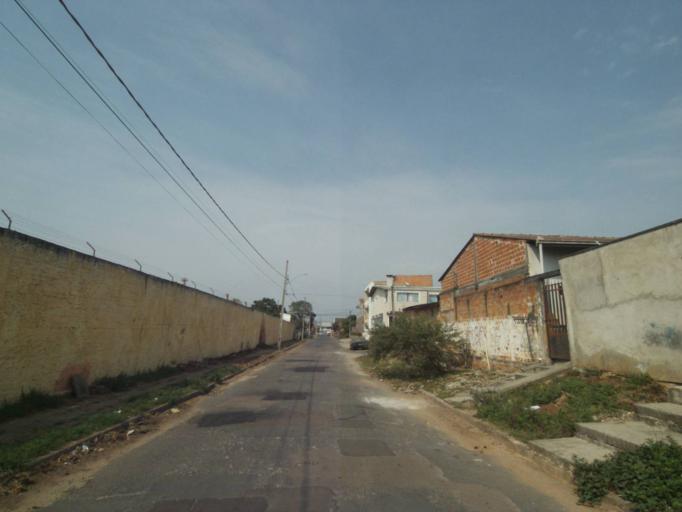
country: BR
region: Parana
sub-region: Pinhais
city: Pinhais
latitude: -25.4850
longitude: -49.2043
